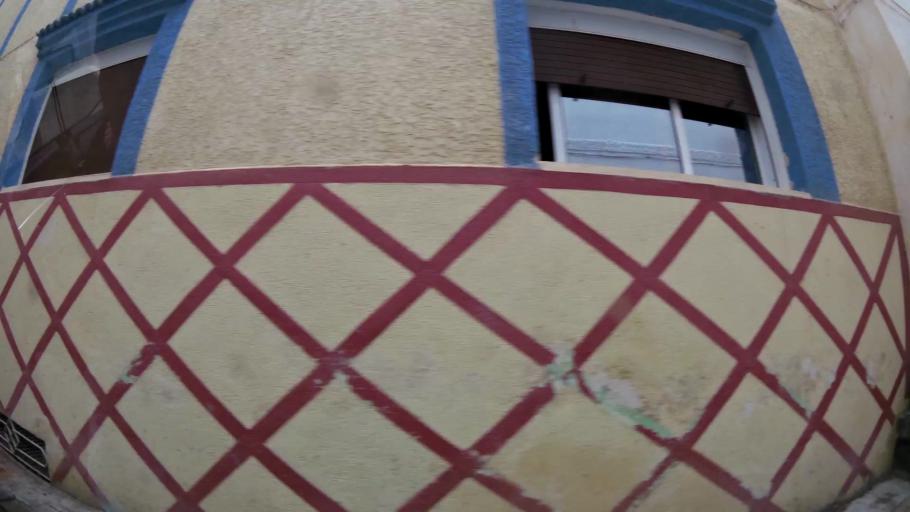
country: MA
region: Taza-Al Hoceima-Taounate
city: Al Hoceima
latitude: 35.2545
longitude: -3.9337
